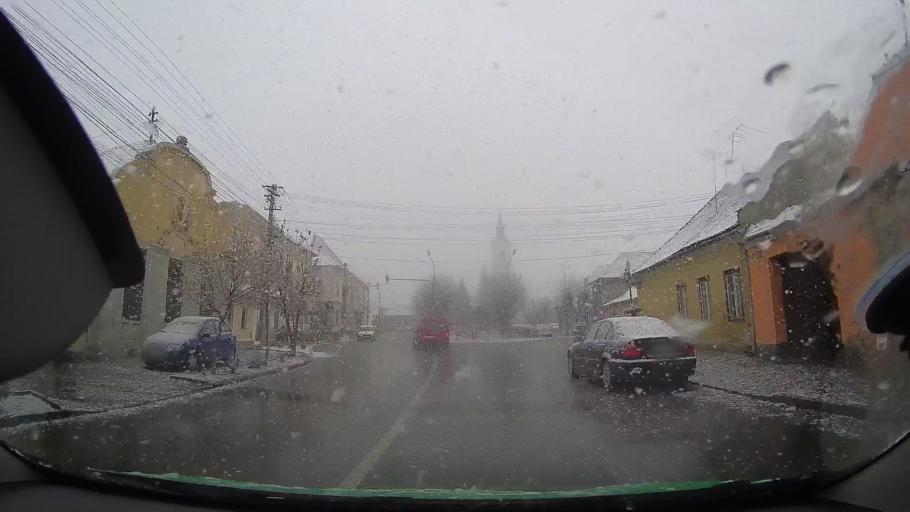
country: RO
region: Sibiu
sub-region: Municipiul Medias
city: Medias
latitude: 46.1673
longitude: 24.3533
